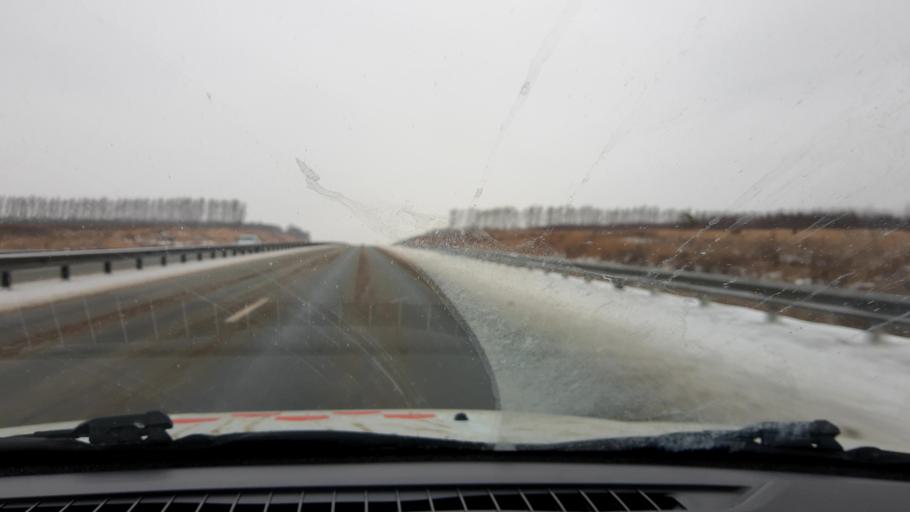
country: RU
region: Nizjnij Novgorod
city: Afonino
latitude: 56.1032
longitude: 44.0129
